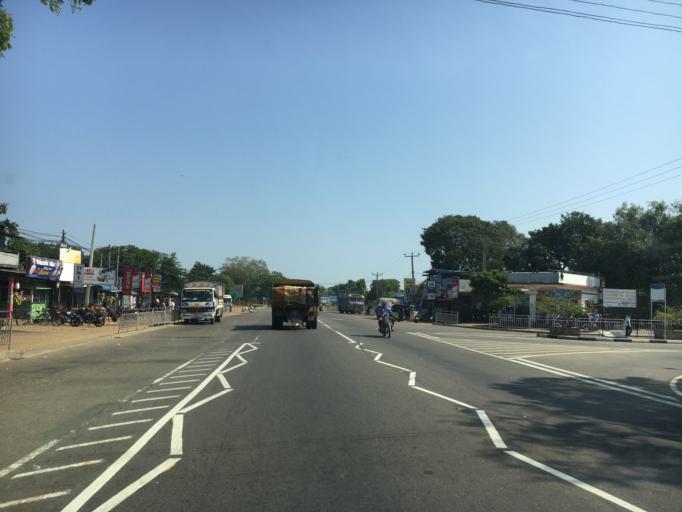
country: LK
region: Northern Province
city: Kilinochchi
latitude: 9.4360
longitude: 80.4077
